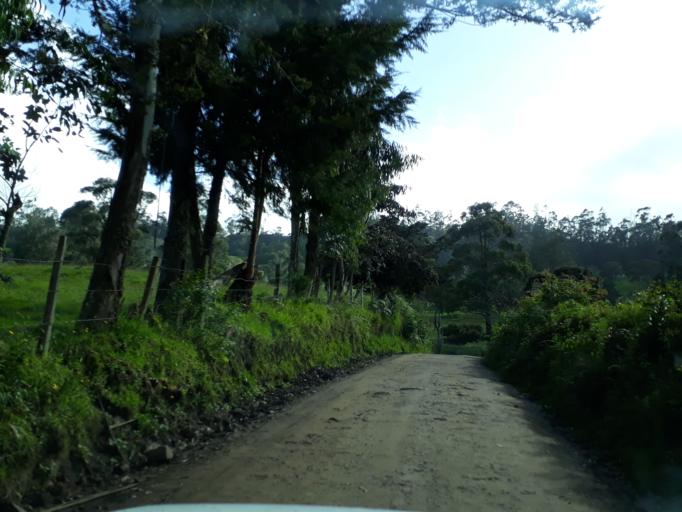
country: CO
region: Cundinamarca
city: Junin
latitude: 4.7906
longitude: -73.6709
